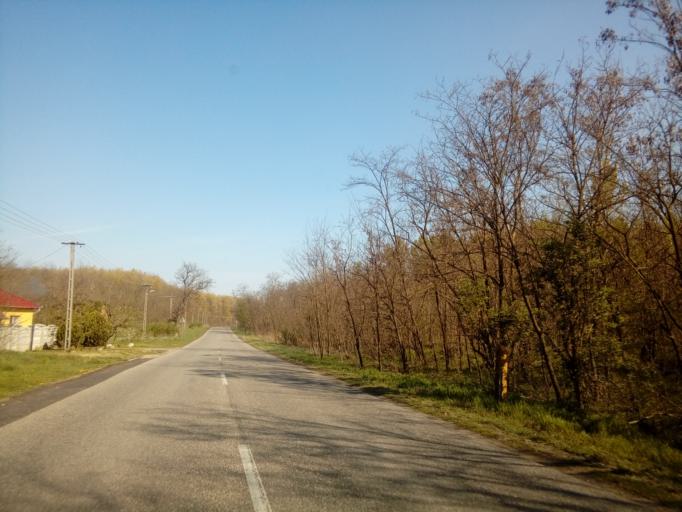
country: HU
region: Szabolcs-Szatmar-Bereg
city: Balkany
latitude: 47.7913
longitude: 21.8532
